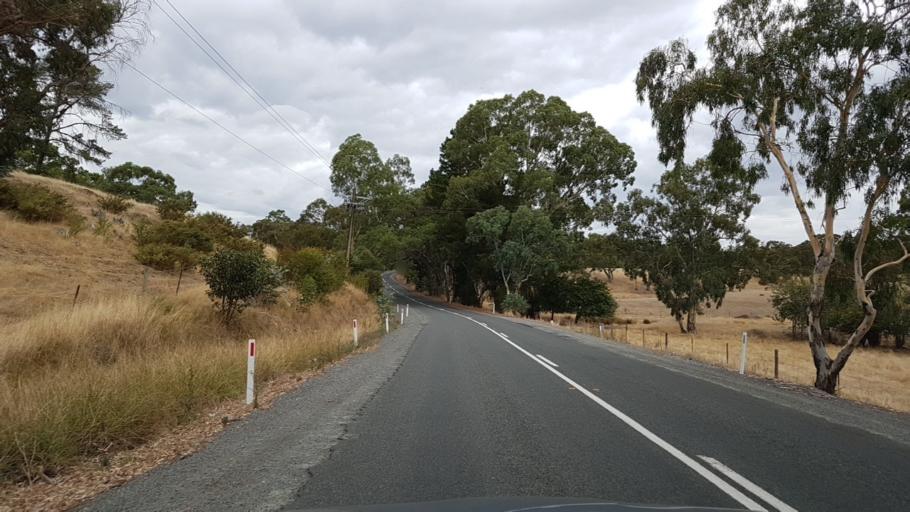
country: AU
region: South Australia
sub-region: Adelaide Hills
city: Gumeracha
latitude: -34.7734
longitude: 138.8679
